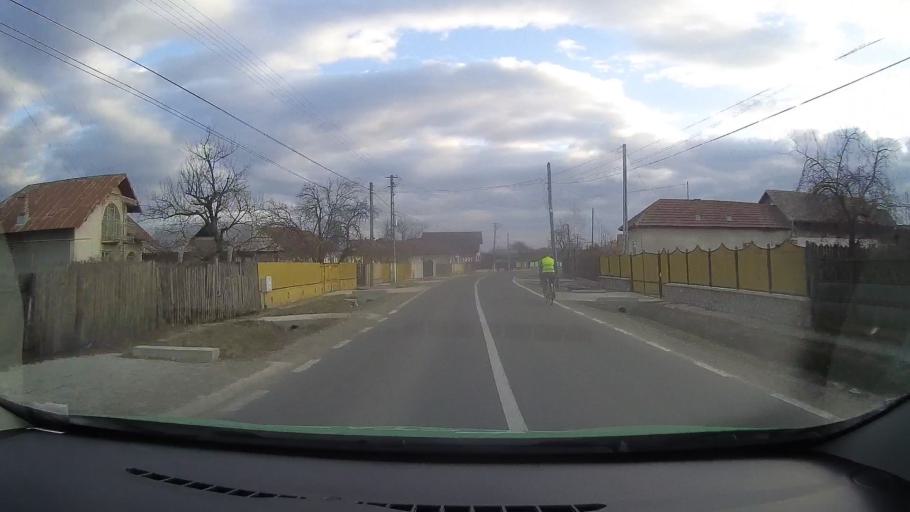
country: RO
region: Dambovita
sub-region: Comuna I. L. Caragiale
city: Mija
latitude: 44.9244
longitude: 25.6907
